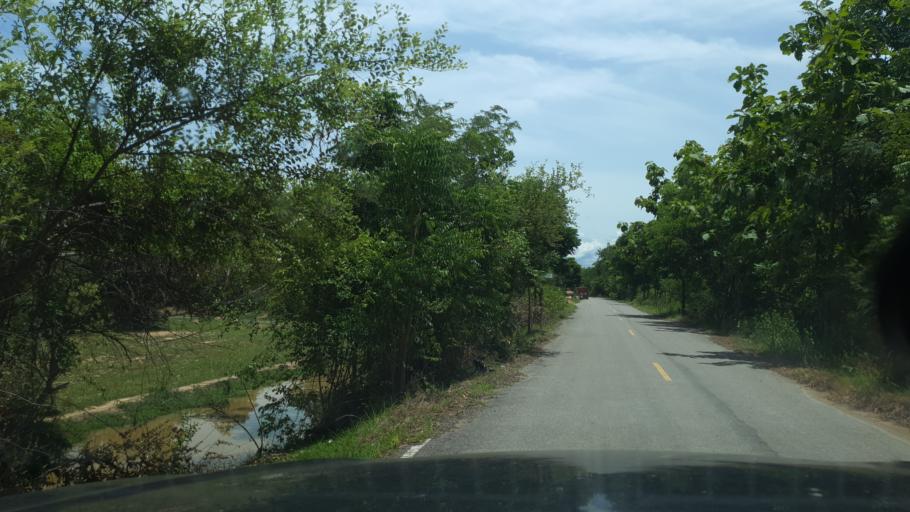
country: TH
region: Sukhothai
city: Ban Na
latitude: 17.1091
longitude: 99.6782
